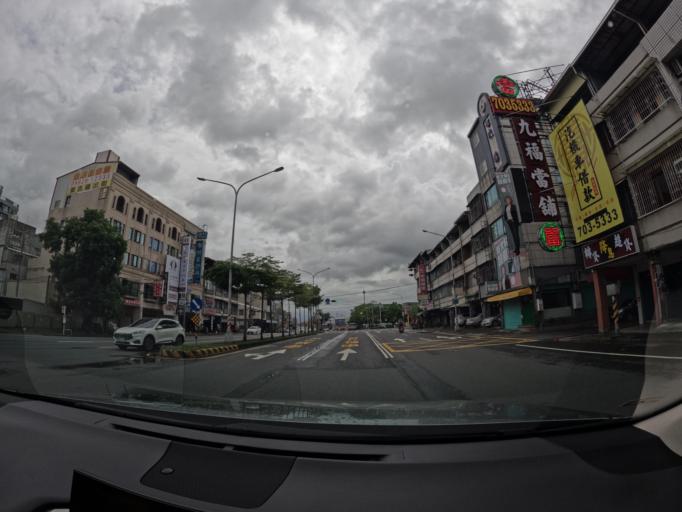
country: TW
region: Taiwan
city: Fengshan
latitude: 22.6284
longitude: 120.3808
